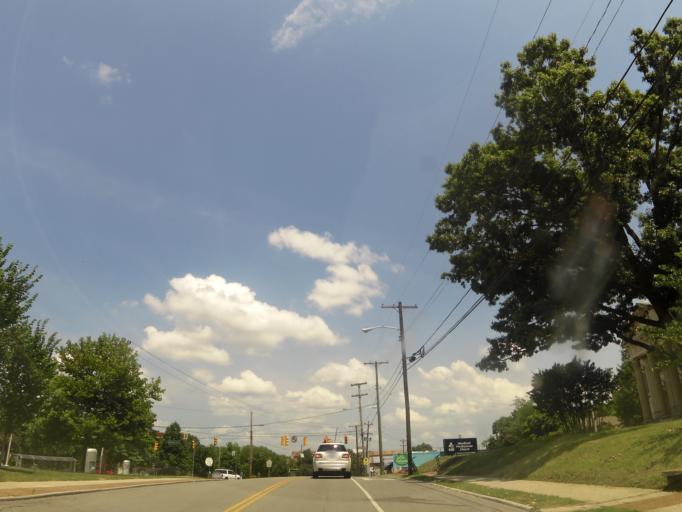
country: US
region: Tennessee
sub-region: Davidson County
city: Nashville
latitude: 36.1790
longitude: -86.7498
